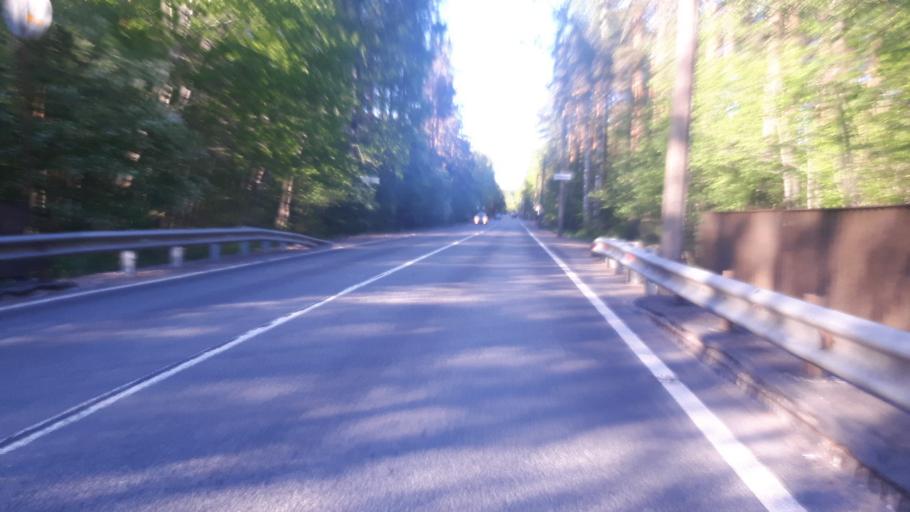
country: RU
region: Leningrad
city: Molodezhnoye
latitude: 60.1753
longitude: 29.4406
